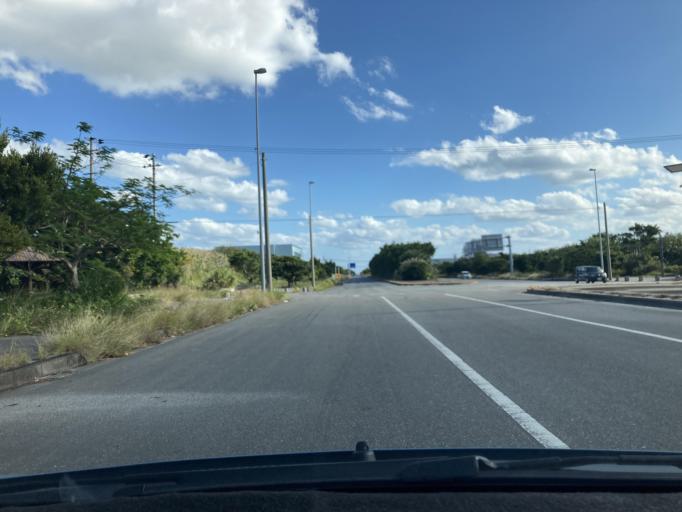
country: JP
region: Okinawa
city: Katsuren-haebaru
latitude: 26.3379
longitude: 127.8617
